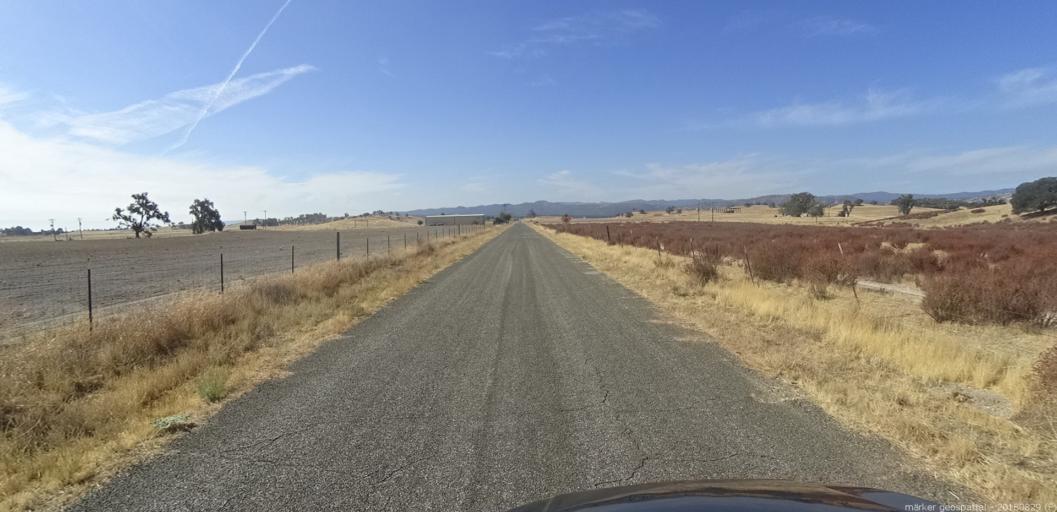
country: US
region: California
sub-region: Monterey County
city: King City
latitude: 35.9684
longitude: -121.1177
